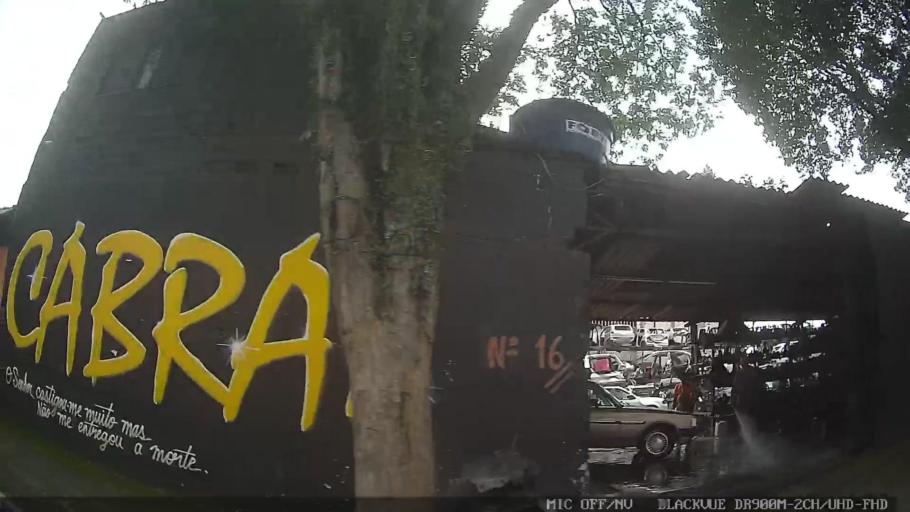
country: BR
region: Sao Paulo
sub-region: Suzano
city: Suzano
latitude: -23.5380
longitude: -46.2999
